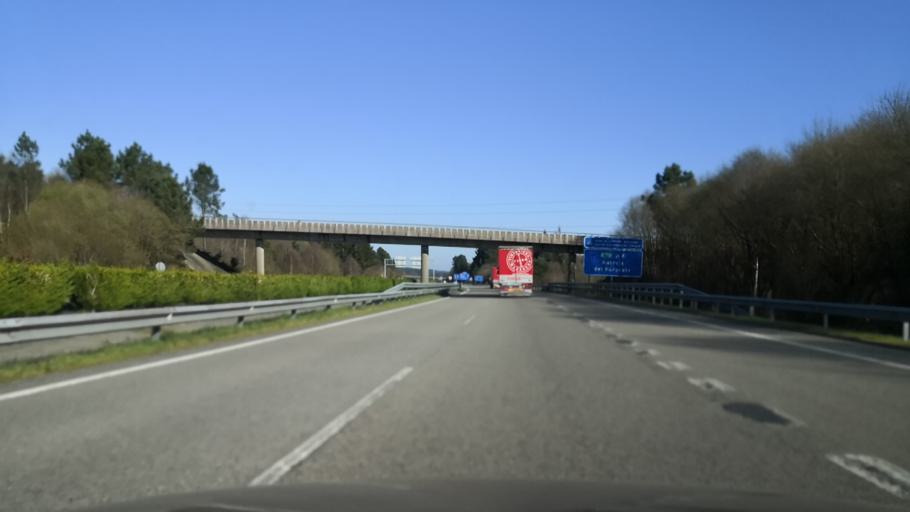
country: ES
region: Galicia
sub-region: Provincia de Lugo
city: Guitiriz
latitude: 43.1928
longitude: -7.9502
